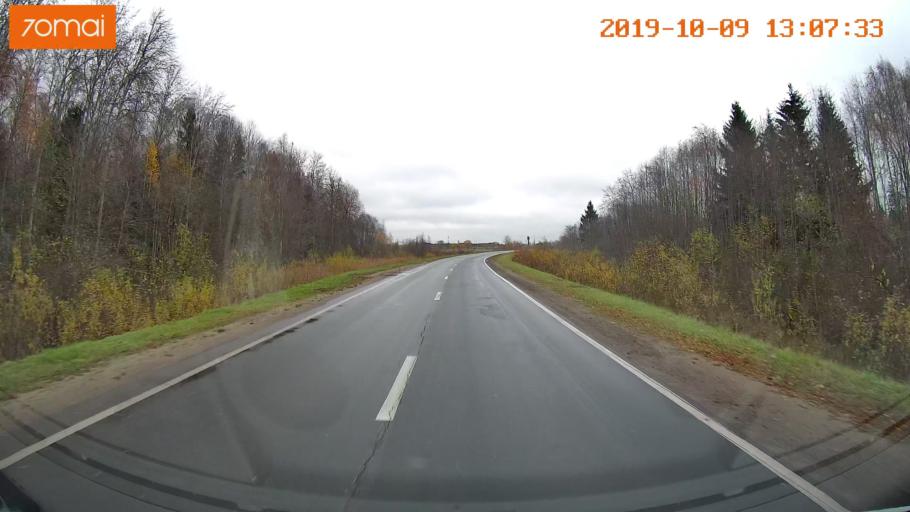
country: RU
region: Jaroslavl
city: Lyubim
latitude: 58.3568
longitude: 40.6443
